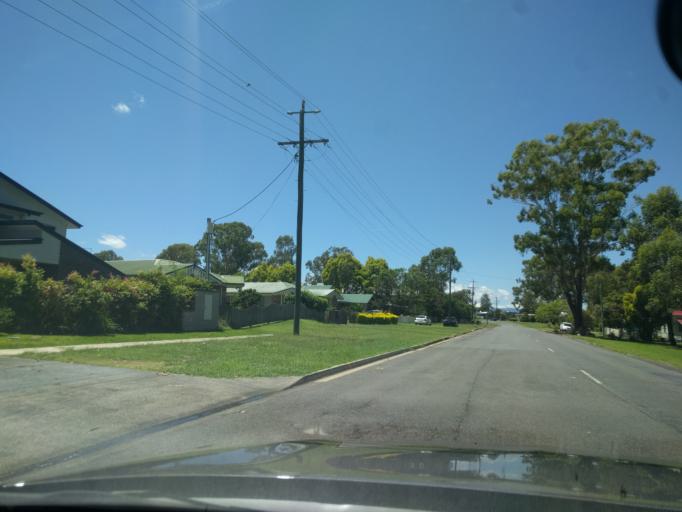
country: AU
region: Queensland
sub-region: Logan
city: Cedar Vale
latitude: -27.9950
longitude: 152.9970
